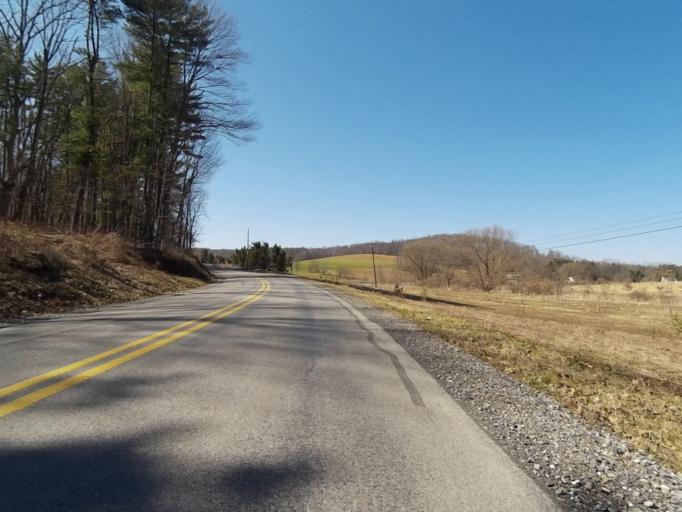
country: US
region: Pennsylvania
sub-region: Centre County
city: Stormstown
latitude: 40.7526
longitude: -78.0356
